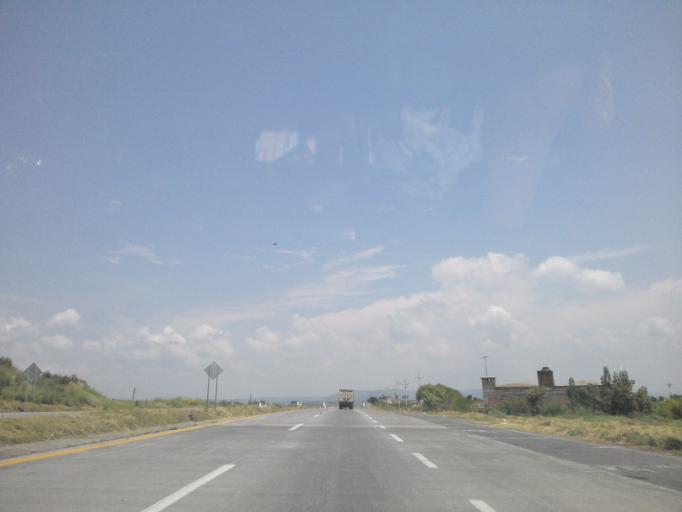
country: MX
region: Jalisco
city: Puente Grande
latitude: 20.5746
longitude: -103.1623
